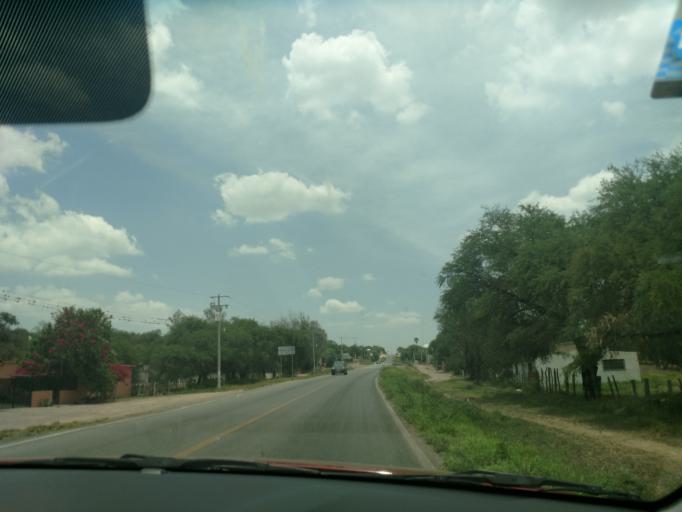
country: MX
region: San Luis Potosi
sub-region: Rioverde
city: Progreso
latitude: 22.0194
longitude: -100.3780
